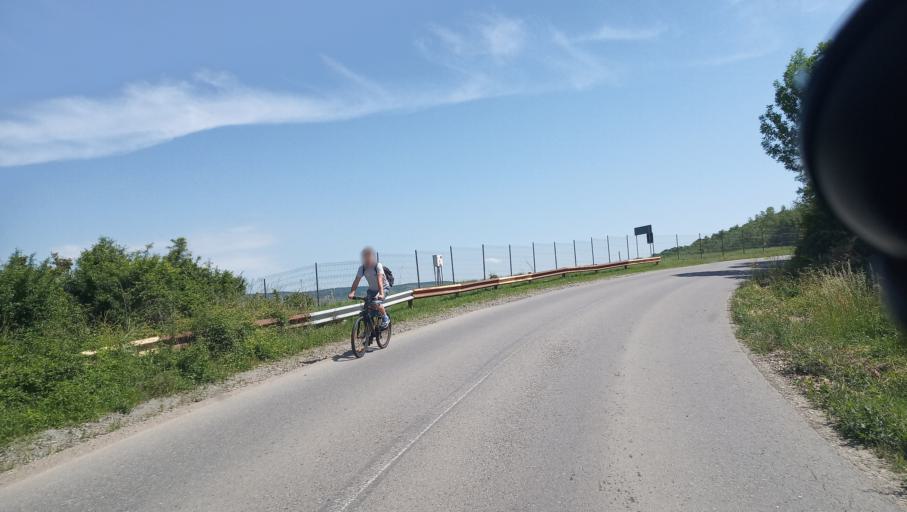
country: RO
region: Cluj
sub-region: Comuna Gilau
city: Gilau
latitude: 46.7382
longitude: 23.3640
